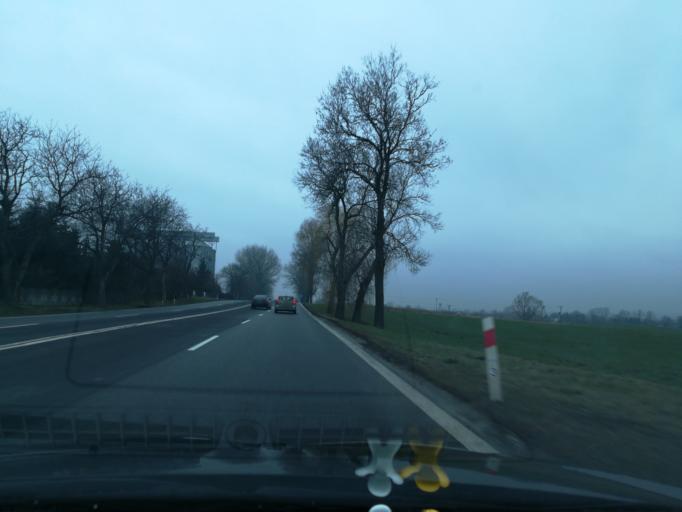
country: PL
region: Subcarpathian Voivodeship
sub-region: Powiat lancucki
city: Gluchow
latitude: 50.0799
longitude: 22.2813
